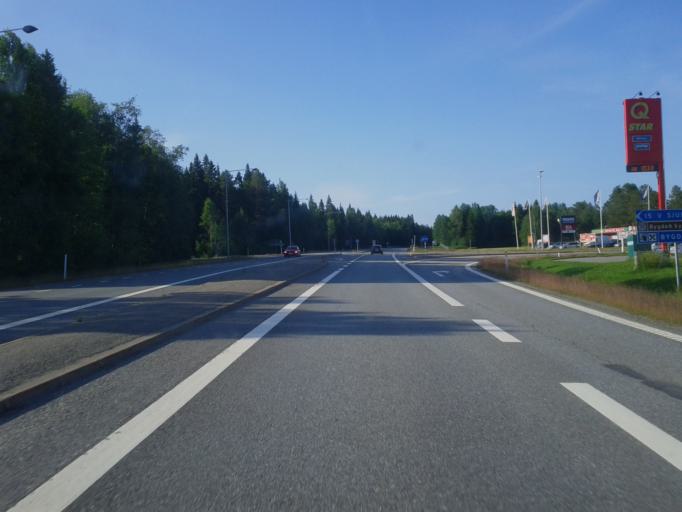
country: SE
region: Vaesterbotten
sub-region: Robertsfors Kommun
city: Robertsfors
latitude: 64.0601
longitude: 20.8477
